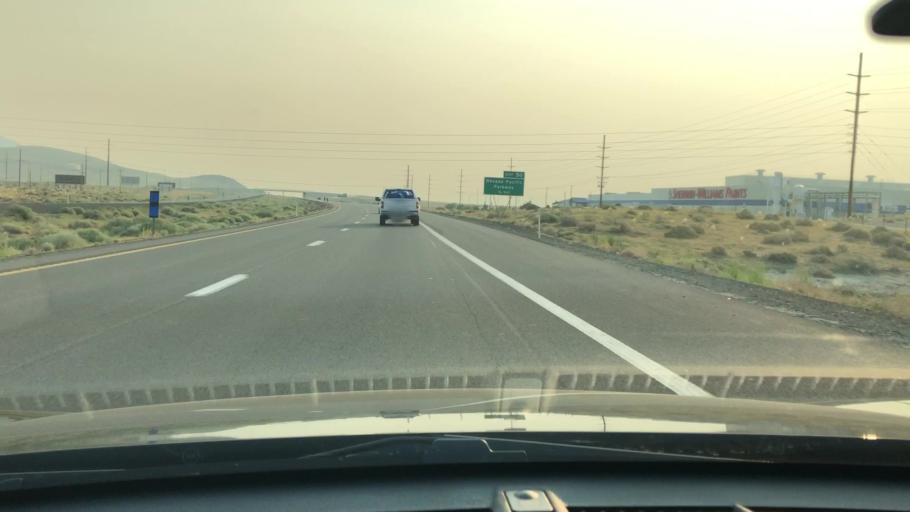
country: US
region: Nevada
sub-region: Lyon County
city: Fernley
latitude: 39.6153
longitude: -119.2116
